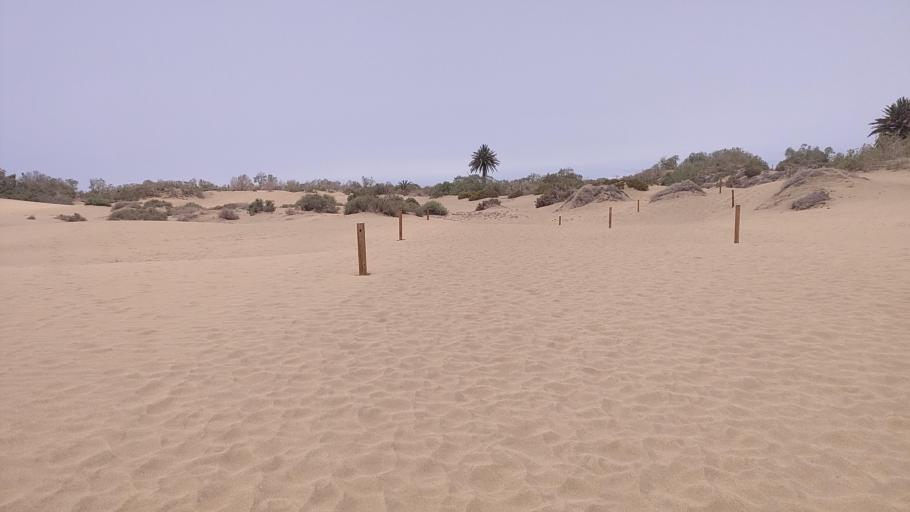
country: ES
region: Canary Islands
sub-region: Provincia de Las Palmas
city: Playa del Ingles
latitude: 27.7448
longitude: -15.5797
